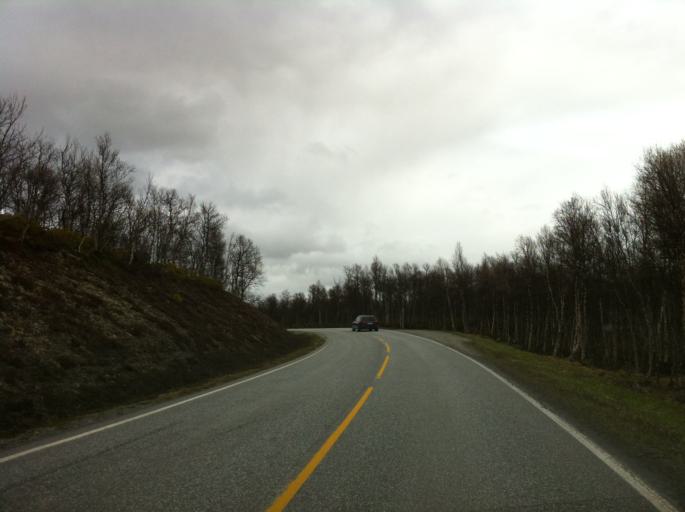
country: NO
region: Sor-Trondelag
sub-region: Roros
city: Roros
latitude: 62.6092
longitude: 11.6255
